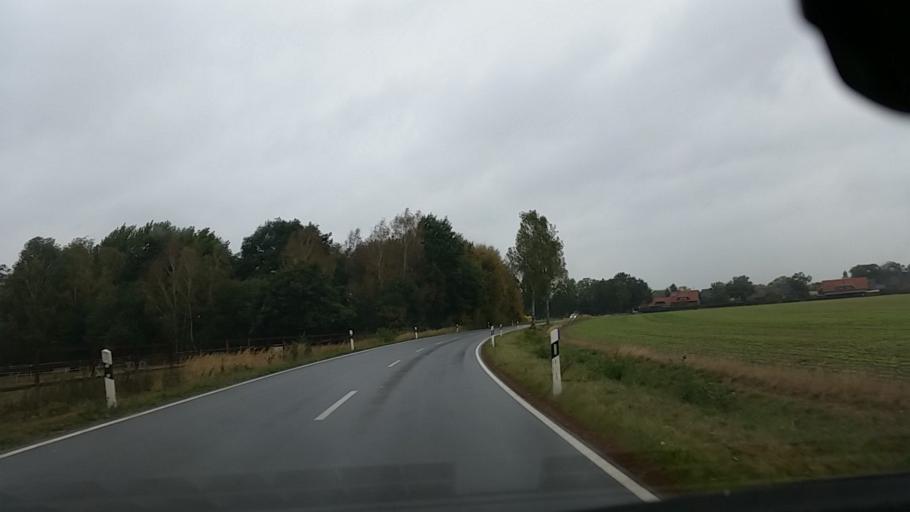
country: DE
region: Lower Saxony
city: Tiddische
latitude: 52.4949
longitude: 10.8007
